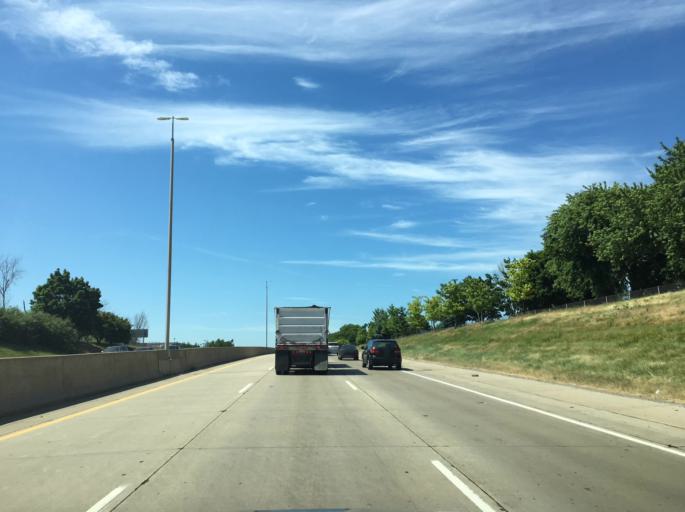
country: US
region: Michigan
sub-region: Wayne County
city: Allen Park
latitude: 42.2839
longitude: -83.2121
